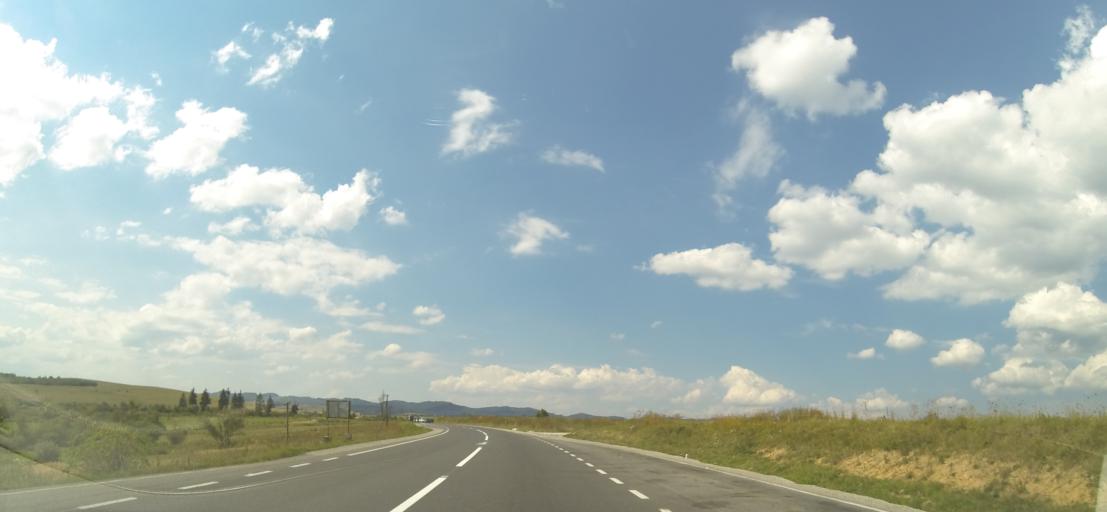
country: RO
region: Brasov
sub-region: Comuna Dumbravita
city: Dumbravita
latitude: 45.7701
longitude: 25.3600
